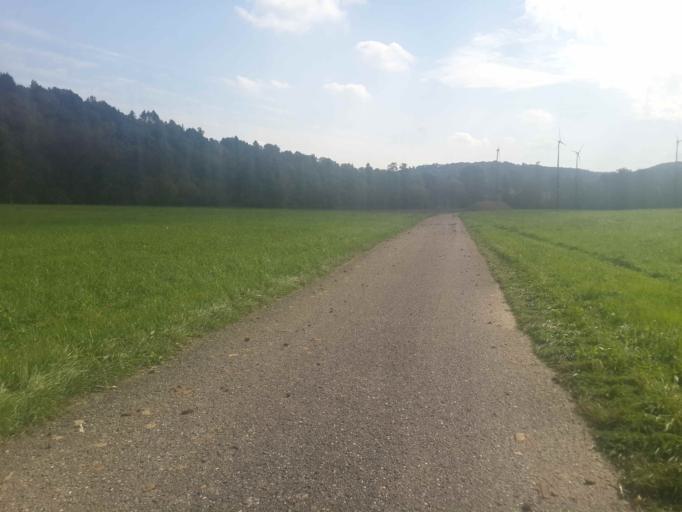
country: DE
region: Baden-Wuerttemberg
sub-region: Regierungsbezirk Stuttgart
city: Widdern
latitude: 49.3144
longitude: 9.4273
